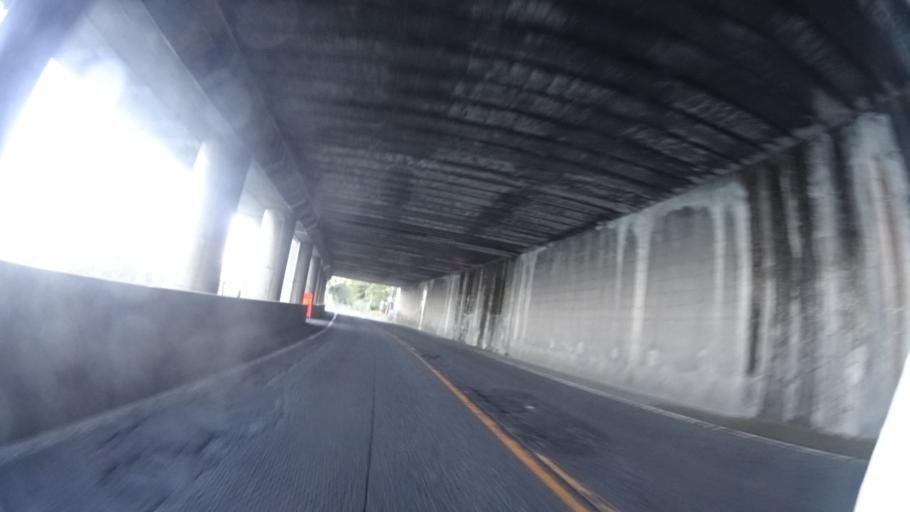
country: JP
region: Fukui
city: Tsuruga
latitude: 35.7314
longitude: 136.0974
